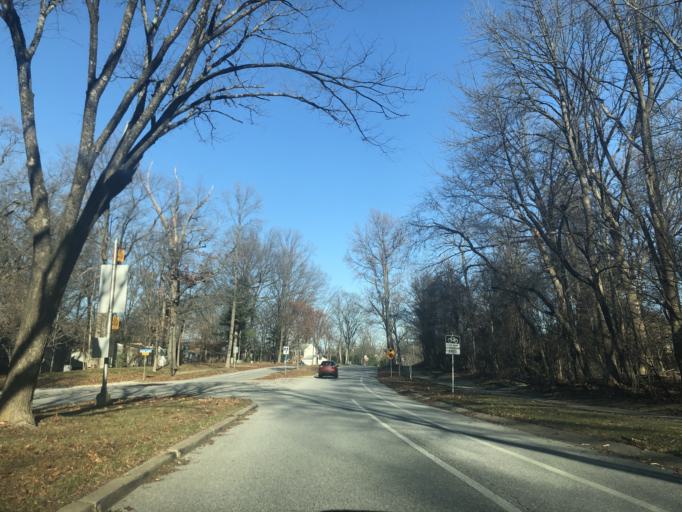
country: US
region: Maryland
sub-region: Howard County
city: Columbia
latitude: 39.2065
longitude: -76.8473
